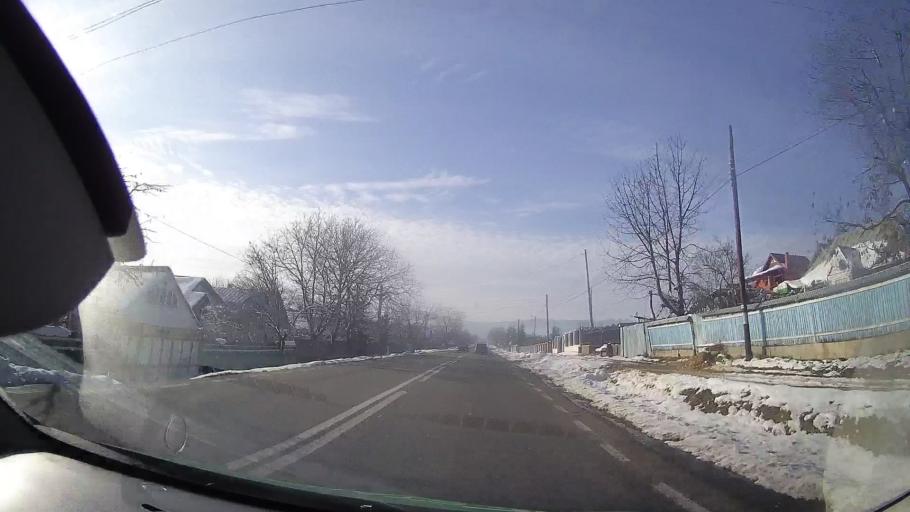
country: RO
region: Neamt
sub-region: Comuna Dobreni
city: Dobreni
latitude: 46.9970
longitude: 26.4049
